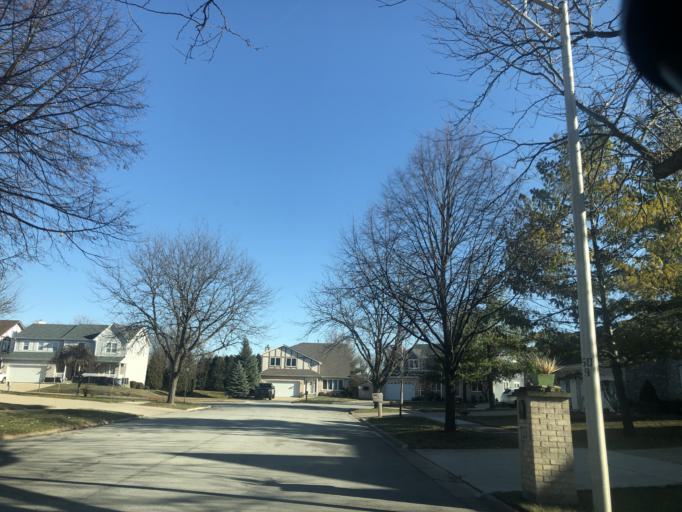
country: US
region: Illinois
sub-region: DuPage County
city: Addison
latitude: 41.9347
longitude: -88.0060
